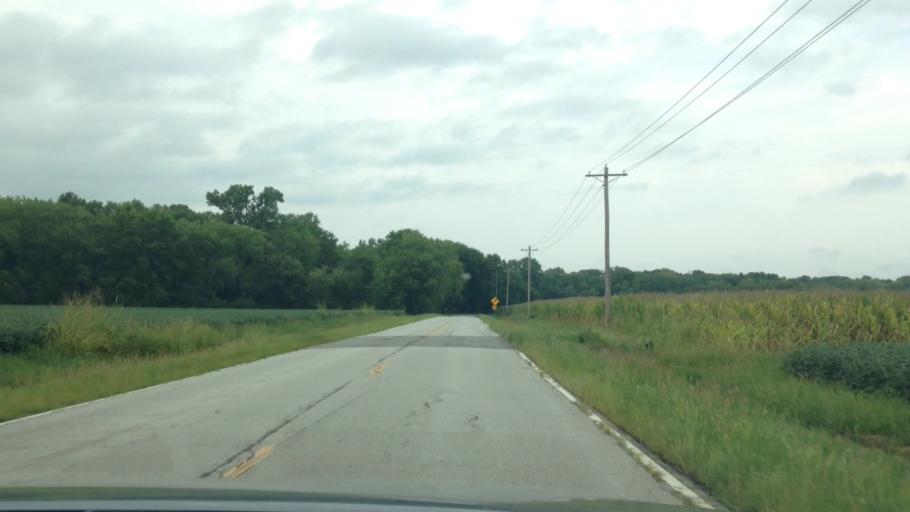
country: US
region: Missouri
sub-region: Clay County
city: Smithville
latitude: 39.4008
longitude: -94.6620
